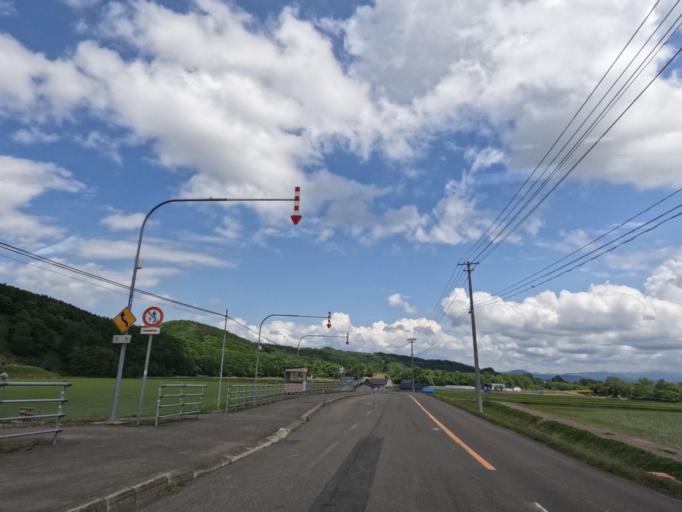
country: JP
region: Hokkaido
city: Takikawa
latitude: 43.5827
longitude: 141.8106
